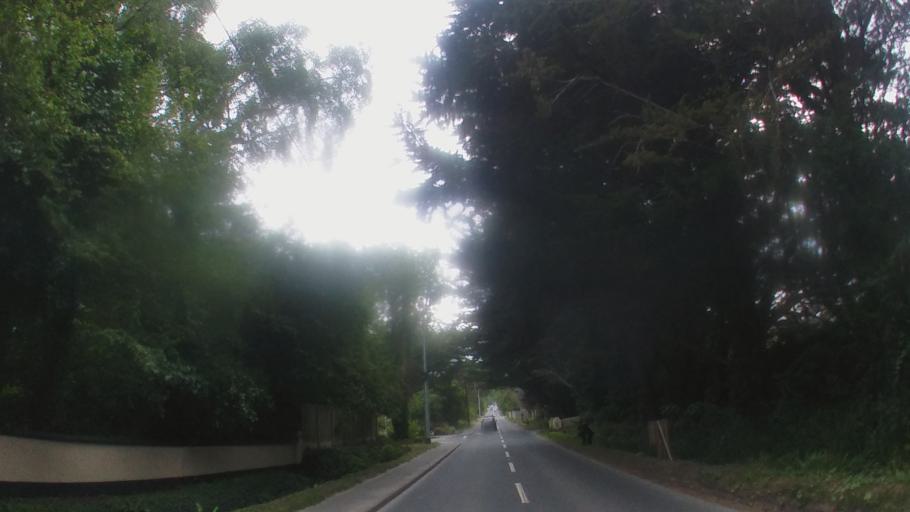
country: IE
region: Leinster
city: Foxrock
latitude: 53.2479
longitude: -6.1825
